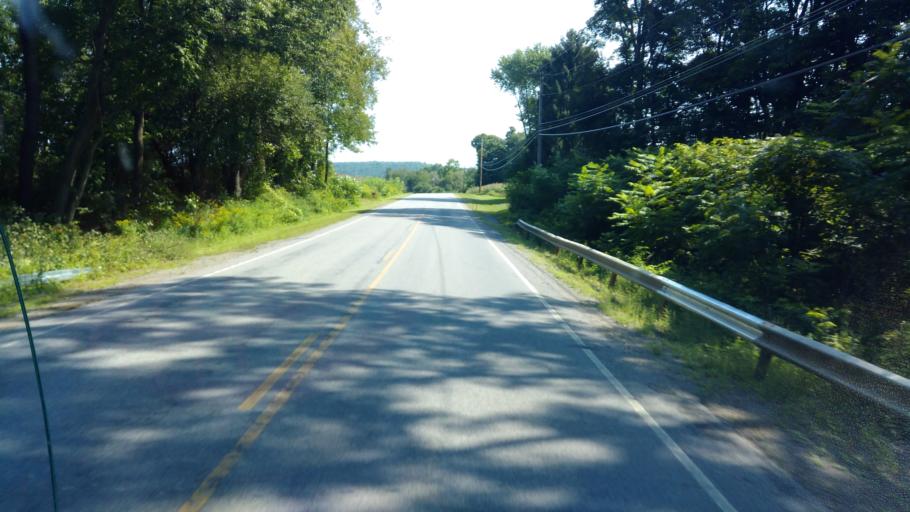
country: US
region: New York
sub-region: Allegany County
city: Friendship
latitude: 42.2206
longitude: -78.0999
